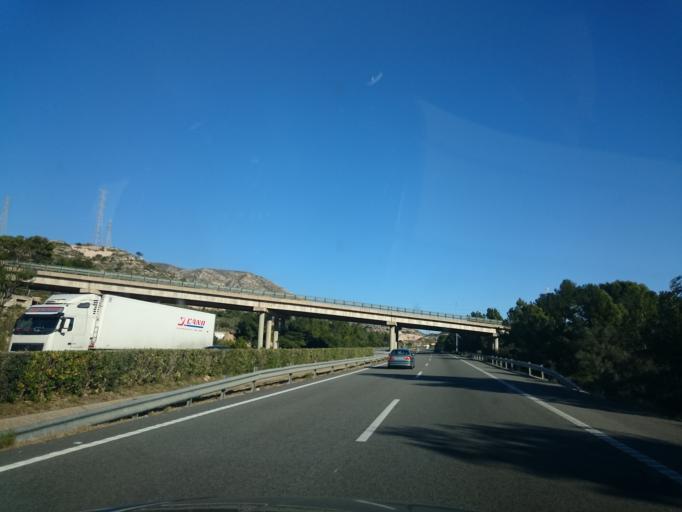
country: ES
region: Catalonia
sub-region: Provincia de Tarragona
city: l'Ametlla de Mar
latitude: 40.9521
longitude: 0.8621
